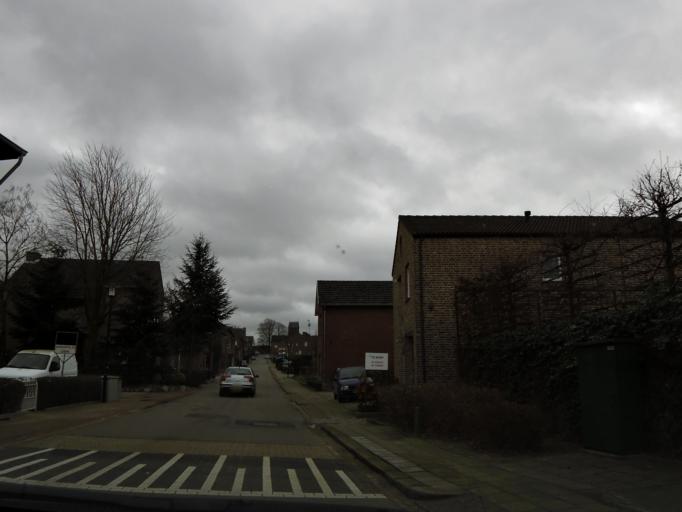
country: NL
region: Limburg
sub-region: Eijsden-Margraten
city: Margraten
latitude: 50.7923
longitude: 5.8064
